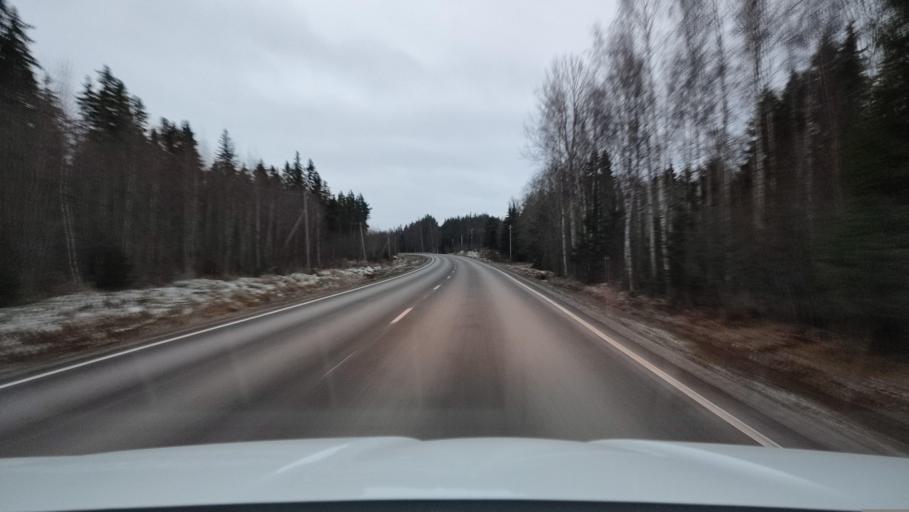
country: FI
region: Ostrobothnia
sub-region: Vaasa
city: Replot
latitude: 63.2126
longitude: 21.4305
